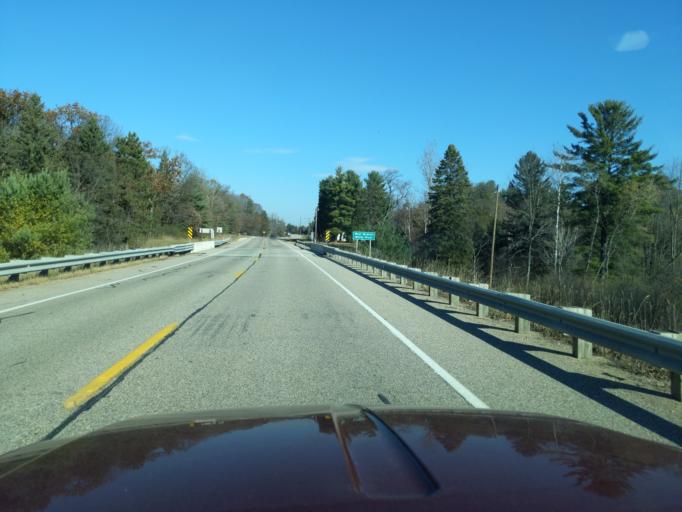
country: US
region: Wisconsin
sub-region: Waushara County
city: Wautoma
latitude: 44.0486
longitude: -89.2949
